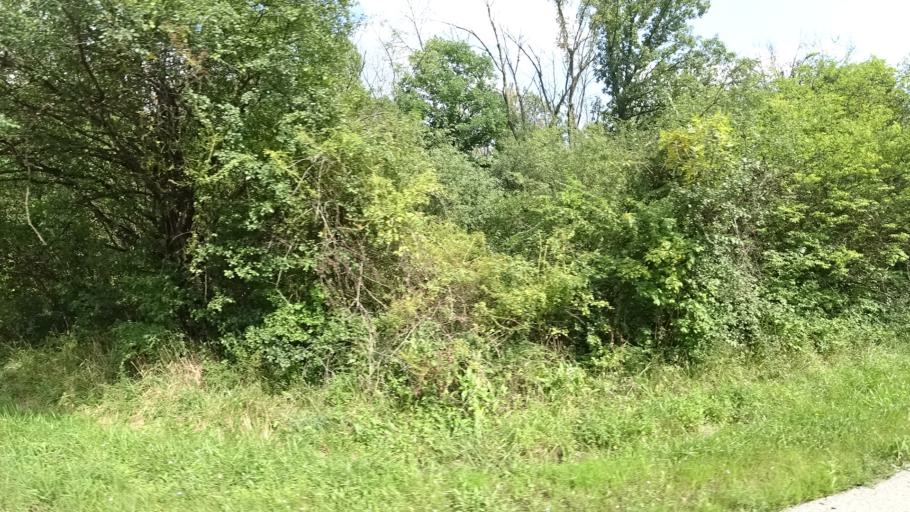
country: US
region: Illinois
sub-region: Will County
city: Goodings Grove
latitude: 41.6650
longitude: -87.9126
